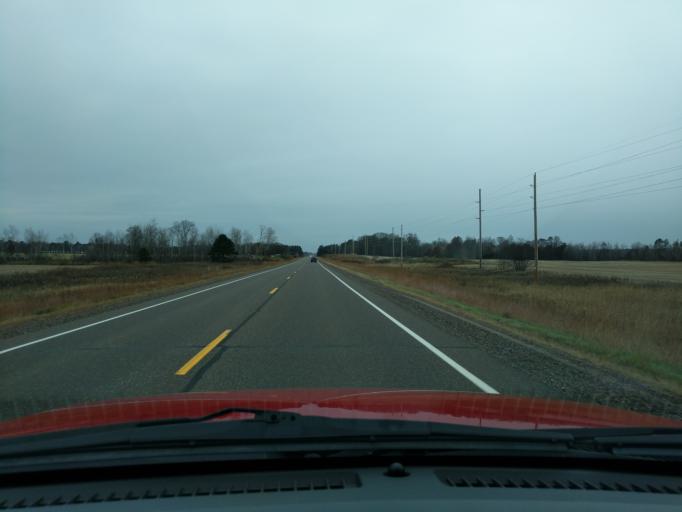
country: US
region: Wisconsin
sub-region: Washburn County
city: Shell Lake
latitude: 45.8154
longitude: -92.0773
